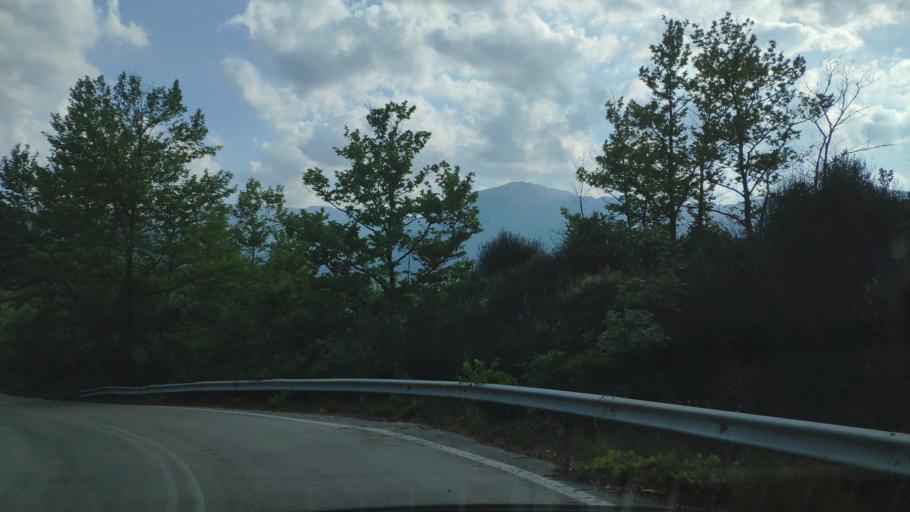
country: GR
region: Epirus
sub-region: Nomos Artas
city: Agios Dimitrios
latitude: 39.4621
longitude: 21.0621
